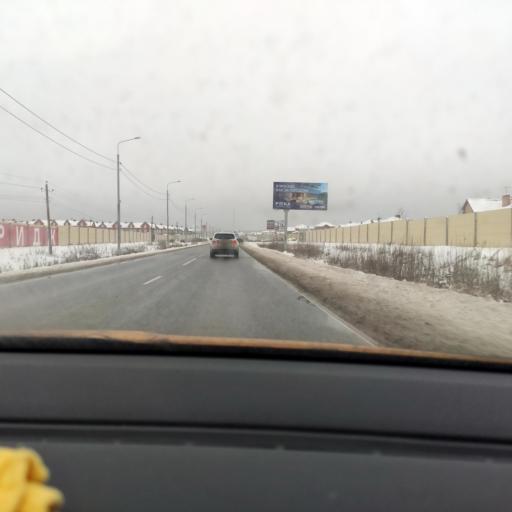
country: RU
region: Moskovskaya
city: Rozhdestveno
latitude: 55.8102
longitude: 36.9880
